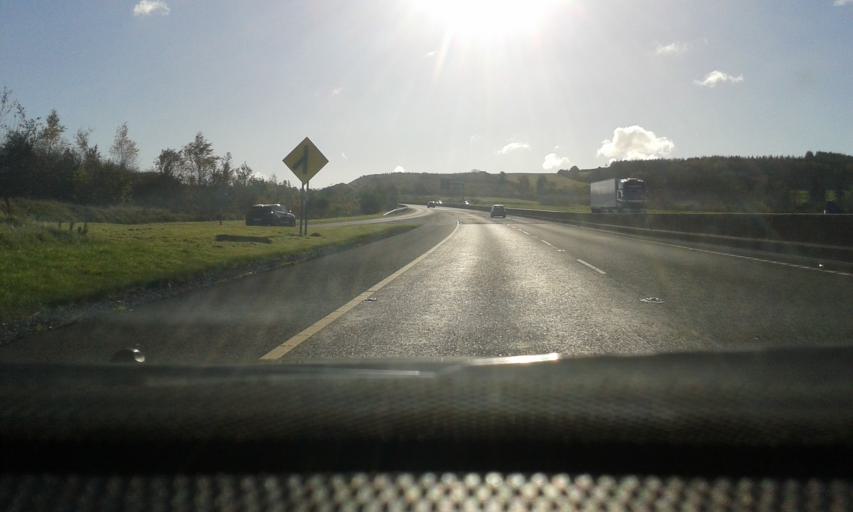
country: IE
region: Munster
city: Cashel
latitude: 52.5414
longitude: -7.8649
